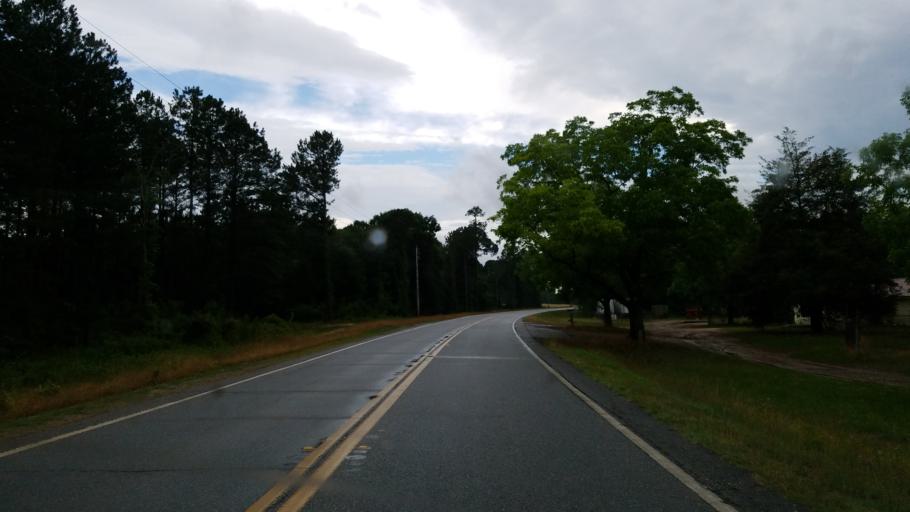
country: US
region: Georgia
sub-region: Crisp County
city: Cordele
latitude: 31.8799
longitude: -83.7675
